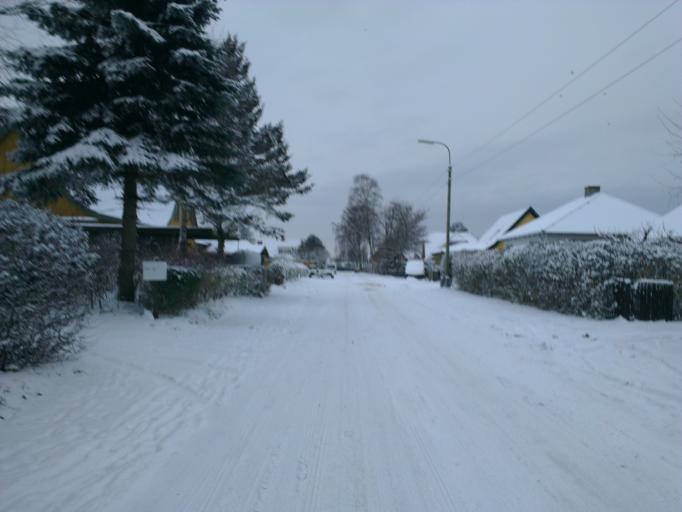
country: DK
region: Capital Region
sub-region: Frederikssund Kommune
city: Jaegerspris
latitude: 55.8531
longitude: 11.9878
